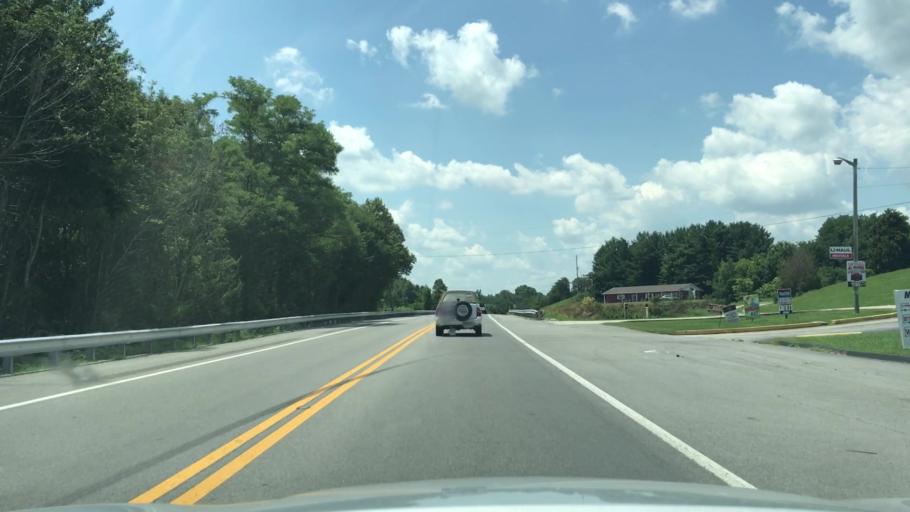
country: US
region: Tennessee
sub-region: Pickett County
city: Byrdstown
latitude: 36.5904
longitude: -85.1249
